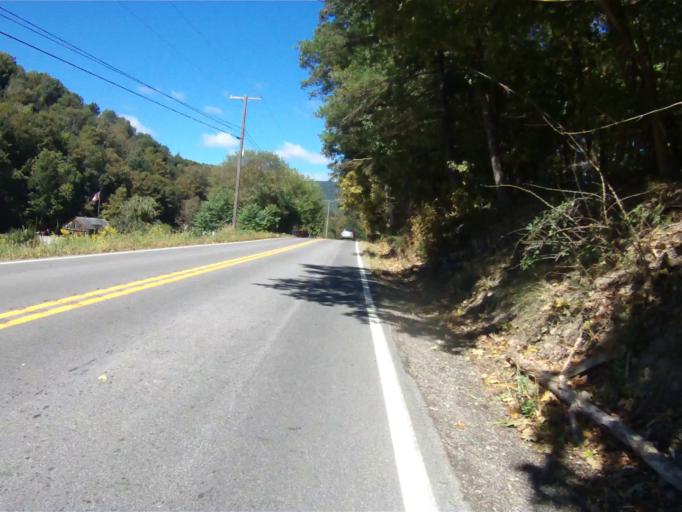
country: US
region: Pennsylvania
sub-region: Centre County
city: Milesburg
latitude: 40.9212
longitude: -77.8965
